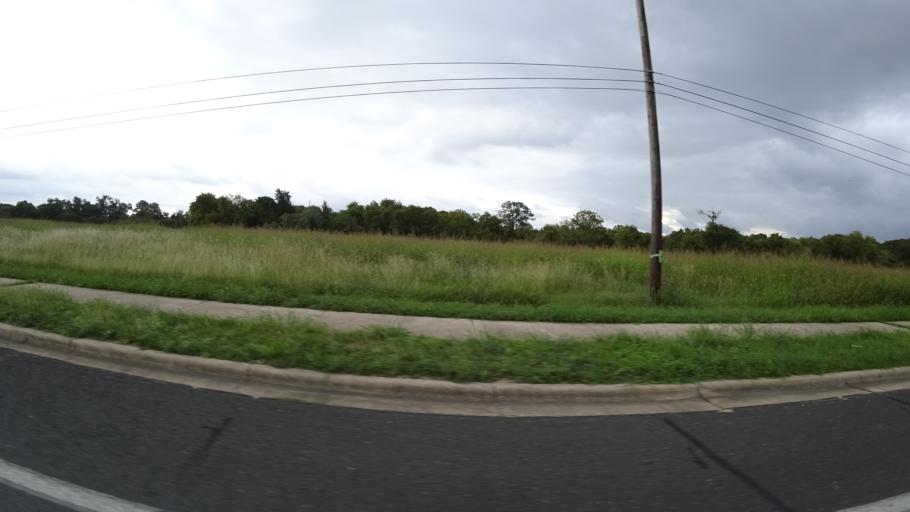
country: US
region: Texas
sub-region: Travis County
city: Onion Creek
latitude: 30.1679
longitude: -97.7378
